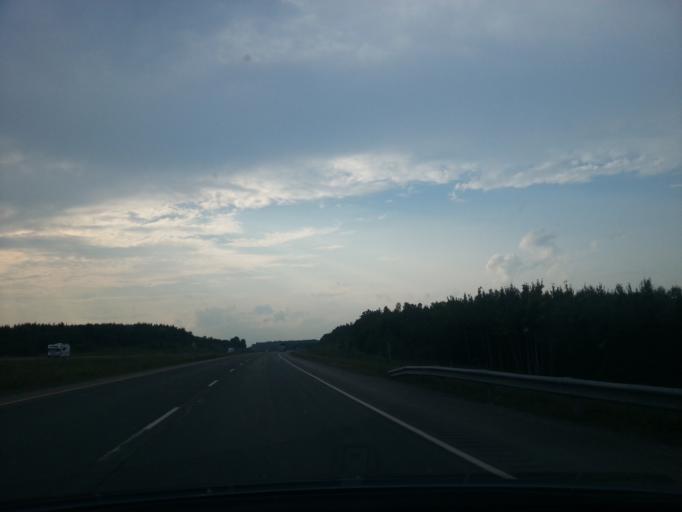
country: CA
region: New Brunswick
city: Harrison Brook
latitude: 47.2924
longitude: -68.0510
